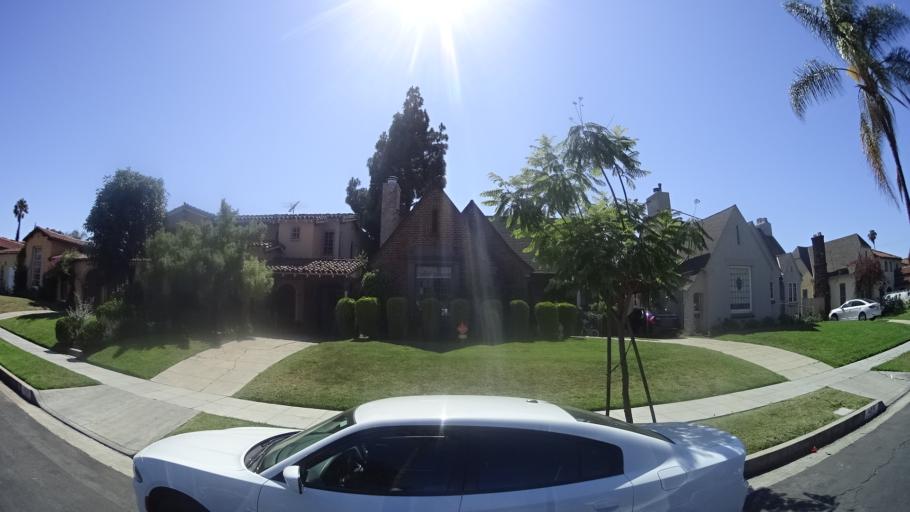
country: US
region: California
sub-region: Los Angeles County
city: West Hollywood
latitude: 34.0750
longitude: -118.3498
